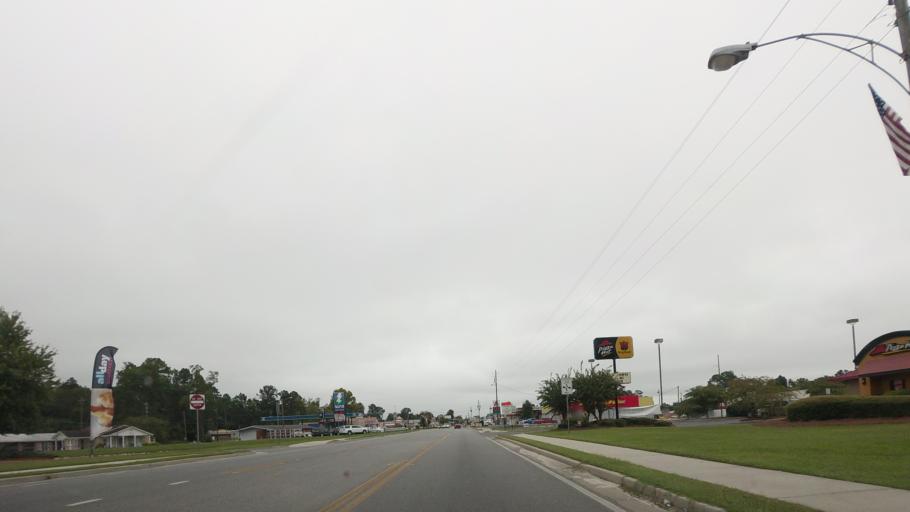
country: US
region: Georgia
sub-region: Berrien County
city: Nashville
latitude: 31.1995
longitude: -83.2511
